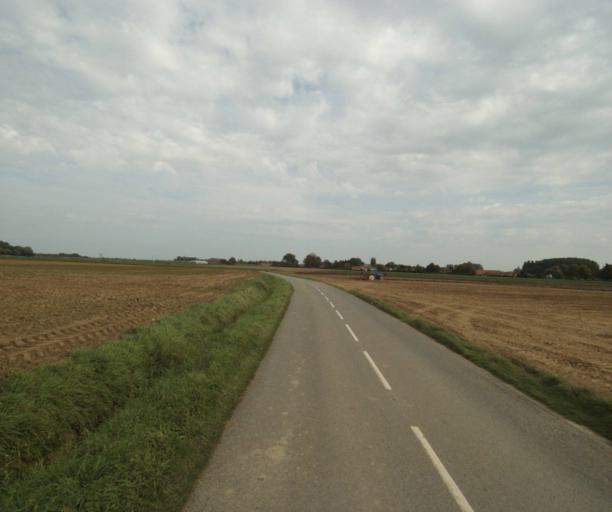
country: FR
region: Nord-Pas-de-Calais
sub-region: Departement du Nord
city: Marquillies
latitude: 50.5588
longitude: 2.8811
